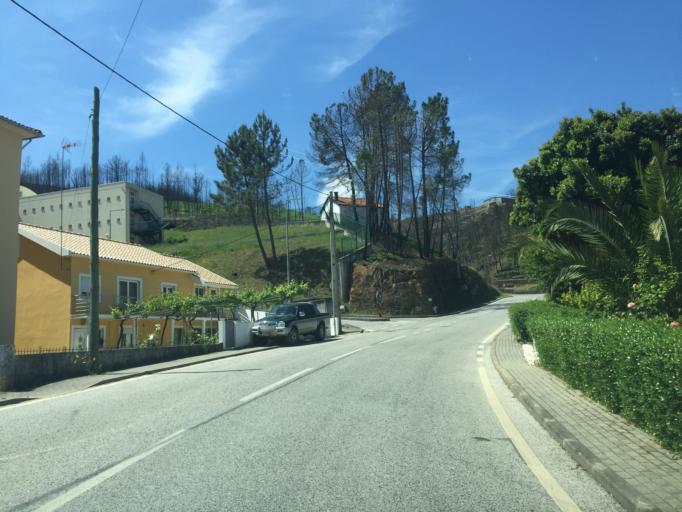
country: PT
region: Coimbra
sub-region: Pampilhosa da Serra
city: Pampilhosa da Serra
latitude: 40.0441
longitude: -7.9503
